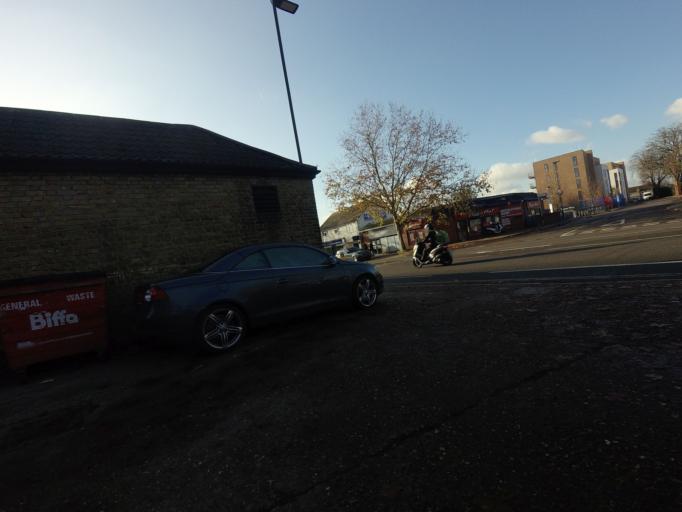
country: GB
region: England
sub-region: Greater London
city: Feltham
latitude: 51.4422
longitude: -0.4129
